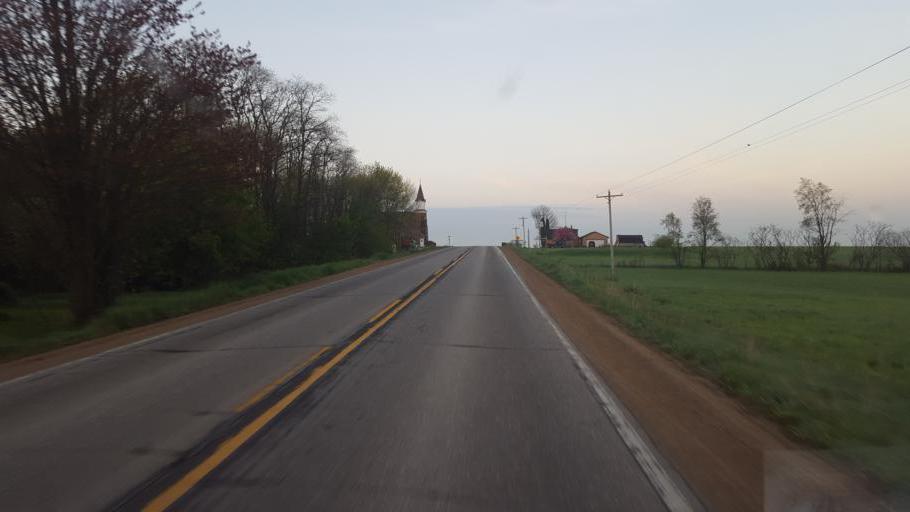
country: US
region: Wisconsin
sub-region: Vernon County
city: Hillsboro
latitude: 43.6248
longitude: -90.4525
